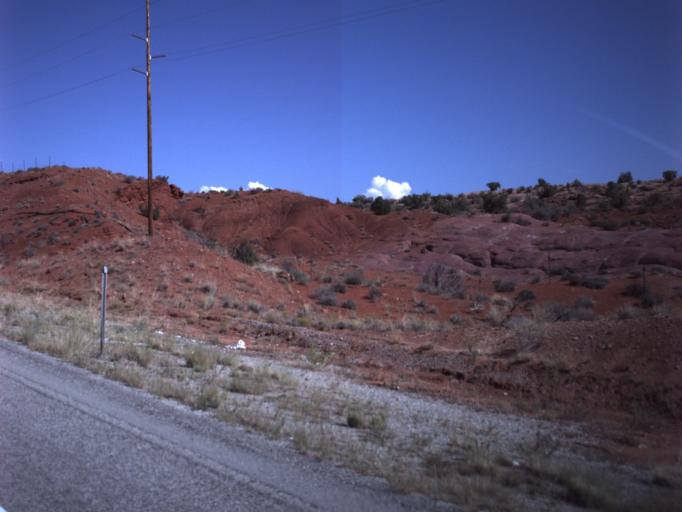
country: US
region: Utah
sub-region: Grand County
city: Moab
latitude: 38.6417
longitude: -109.6676
